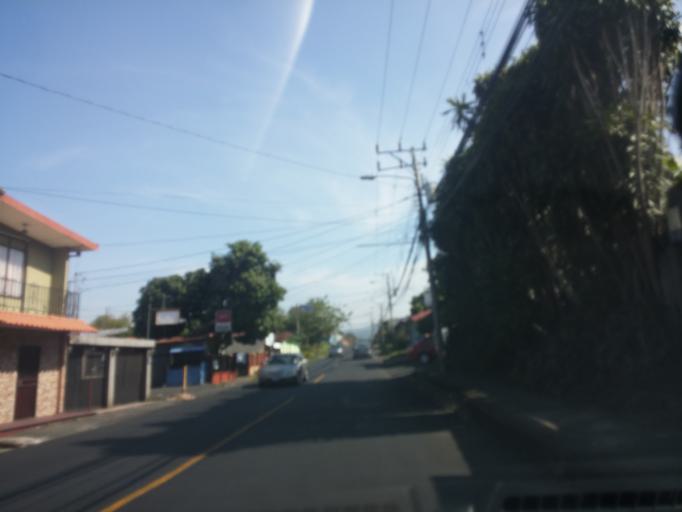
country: CR
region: Heredia
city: Llorente
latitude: 10.0136
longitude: -84.1540
